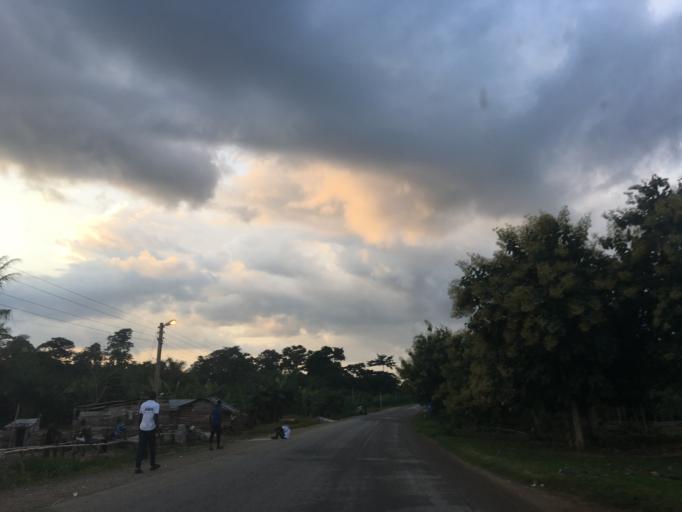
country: GH
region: Western
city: Bibiani
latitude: 6.7502
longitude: -2.5045
